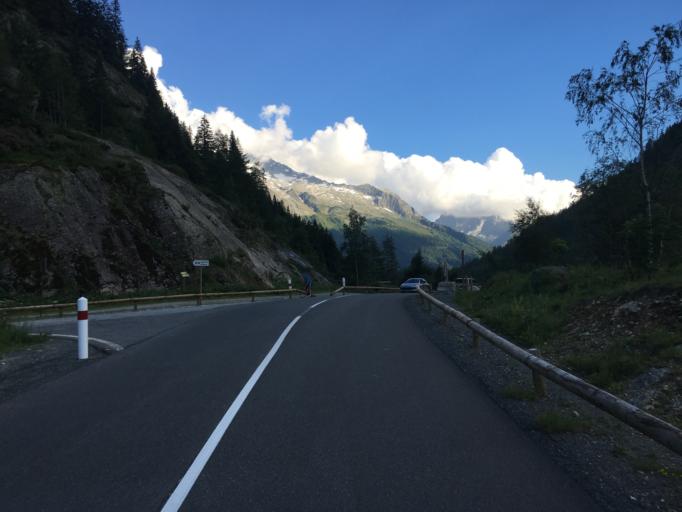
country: FR
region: Rhone-Alpes
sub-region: Departement de la Haute-Savoie
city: Chamonix-Mont-Blanc
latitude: 46.0046
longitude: 6.9237
